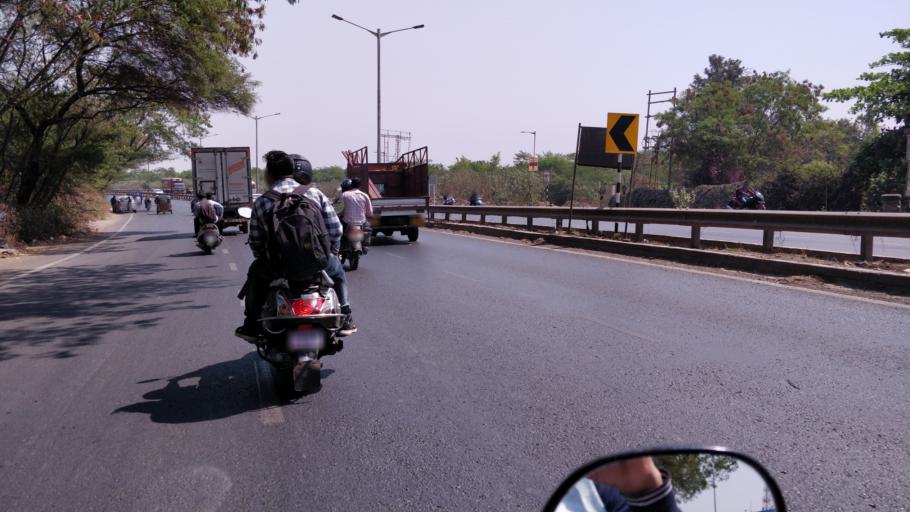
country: IN
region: Maharashtra
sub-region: Pune Division
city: Shivaji Nagar
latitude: 18.5280
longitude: 73.7773
